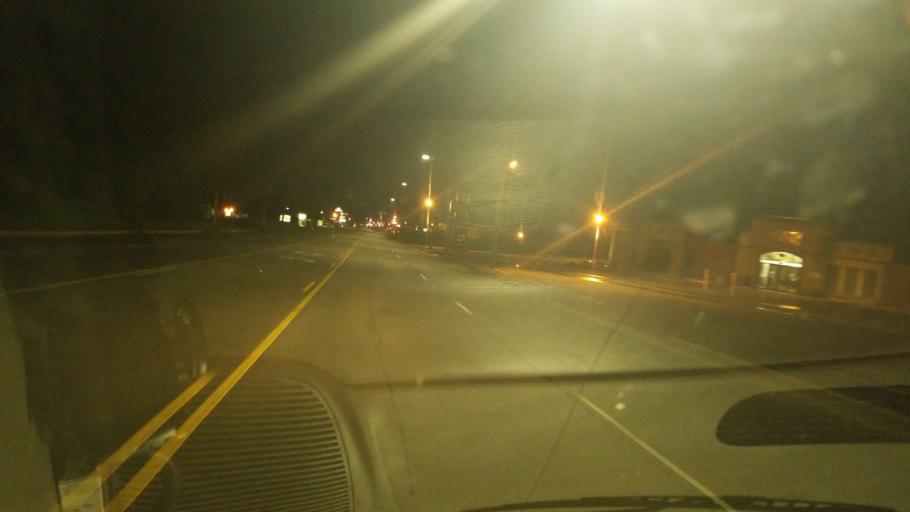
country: US
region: Ohio
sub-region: Trumbull County
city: McKinley Heights
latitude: 41.2023
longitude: -80.7357
